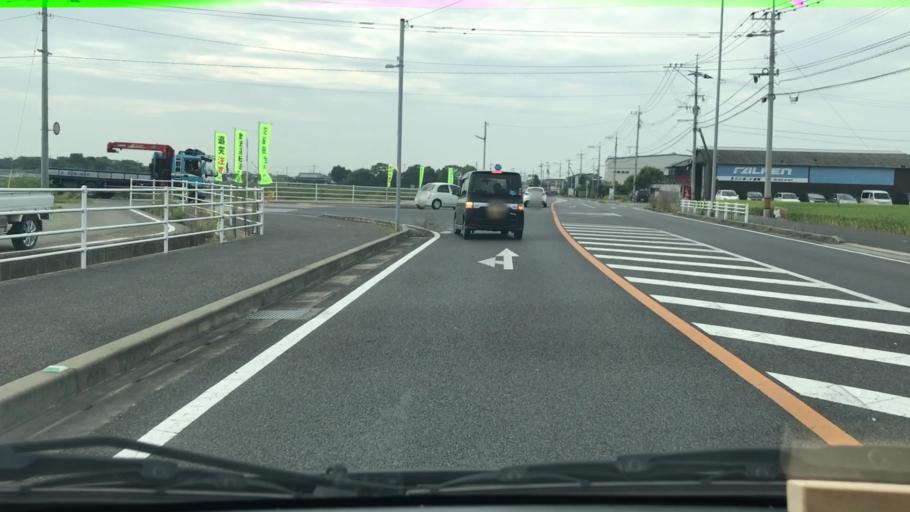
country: JP
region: Saga Prefecture
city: Saga-shi
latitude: 33.2277
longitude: 130.2576
